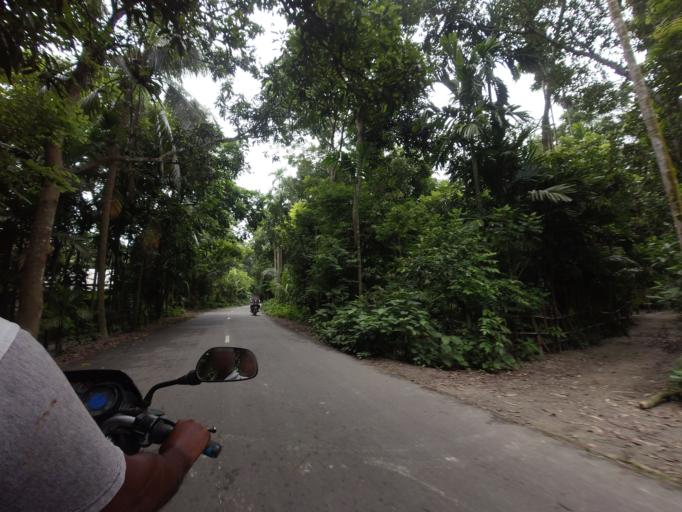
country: BD
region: Khulna
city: Kalia
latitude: 23.1356
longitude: 89.6440
